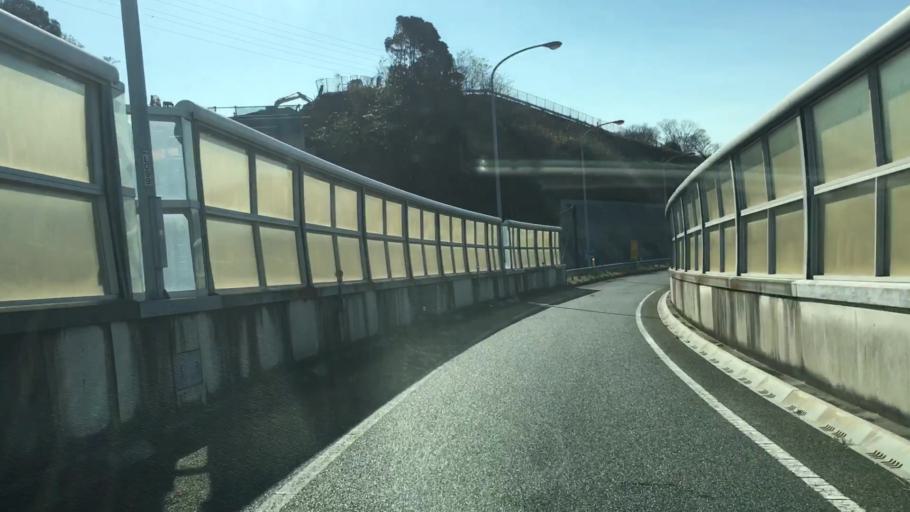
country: JP
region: Kanagawa
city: Miura
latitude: 35.2129
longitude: 139.6372
